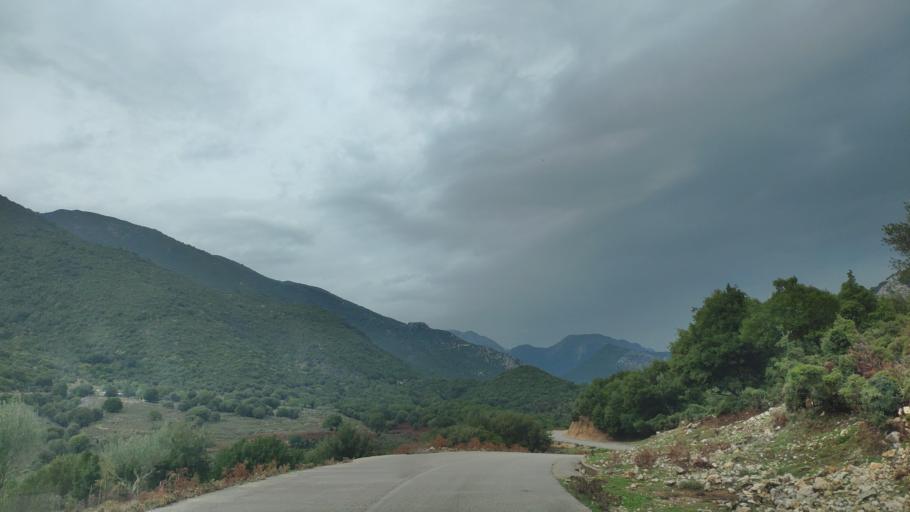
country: GR
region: Epirus
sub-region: Nomos Thesprotias
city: Paramythia
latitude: 39.3859
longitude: 20.6244
